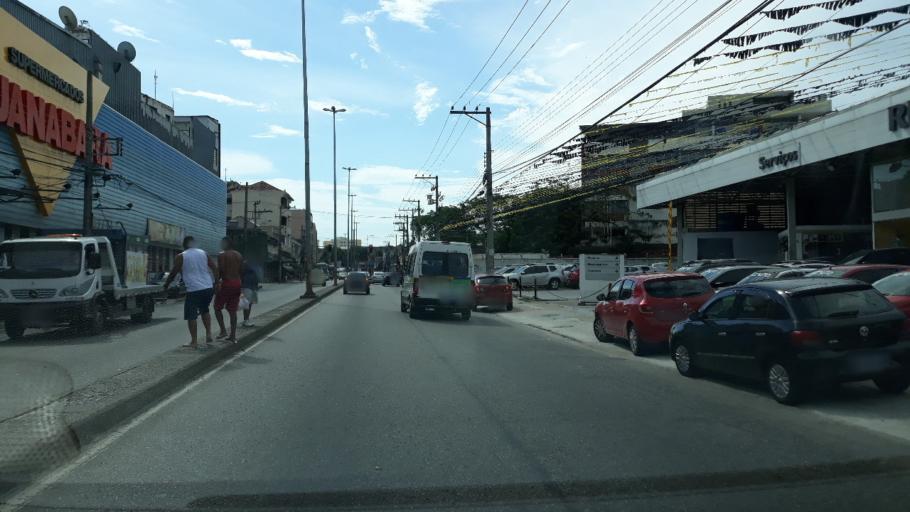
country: BR
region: Rio de Janeiro
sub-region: Duque De Caxias
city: Duque de Caxias
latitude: -22.8862
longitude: -43.3081
